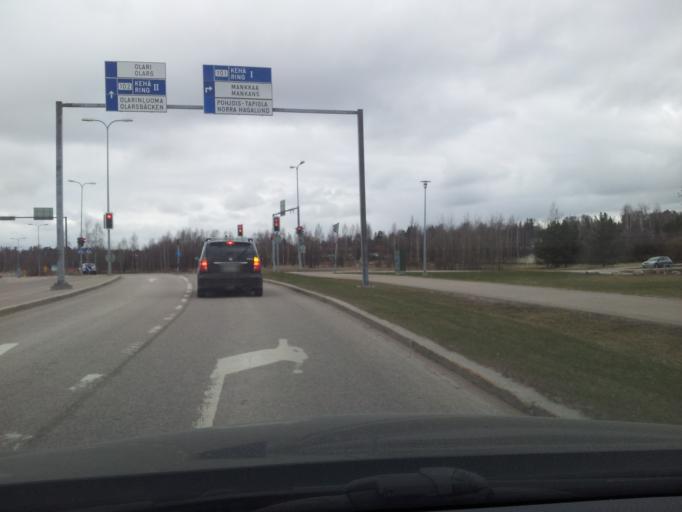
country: FI
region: Uusimaa
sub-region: Helsinki
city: Koukkuniemi
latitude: 60.1812
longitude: 24.7799
